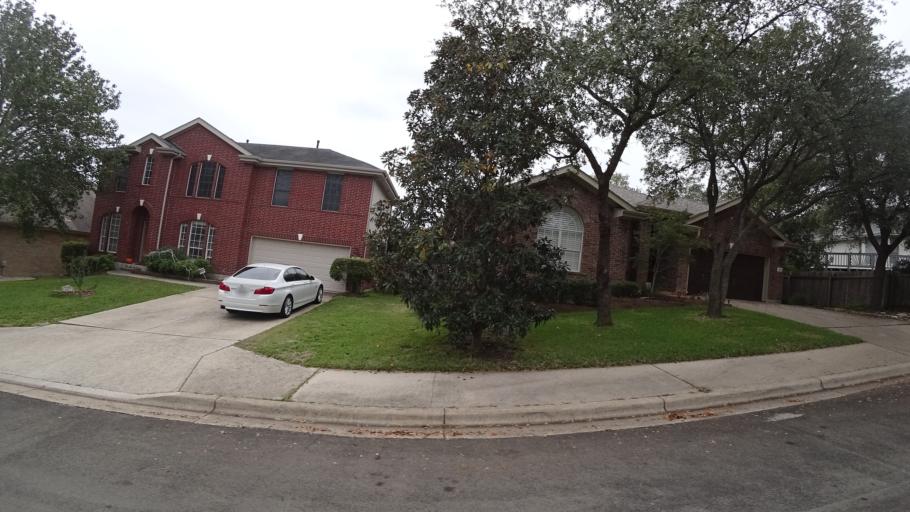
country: US
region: Texas
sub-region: Travis County
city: Shady Hollow
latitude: 30.2151
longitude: -97.8861
